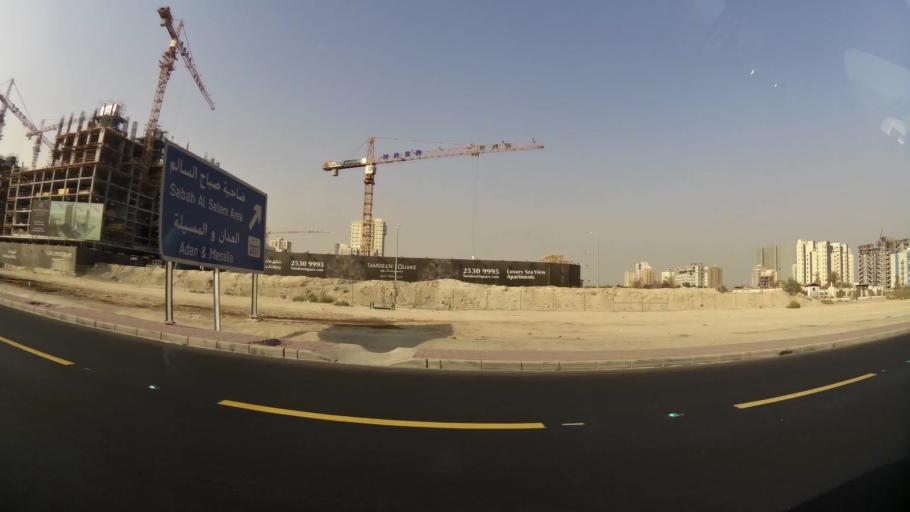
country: KW
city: Al Funaytis
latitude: 29.2535
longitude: 48.0900
